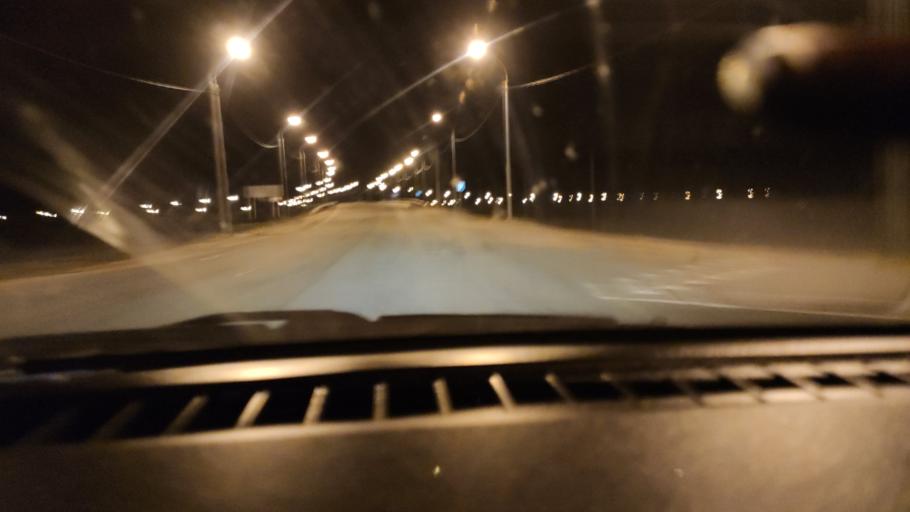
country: RU
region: Samara
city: Varlamovo
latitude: 53.1939
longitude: 48.2929
